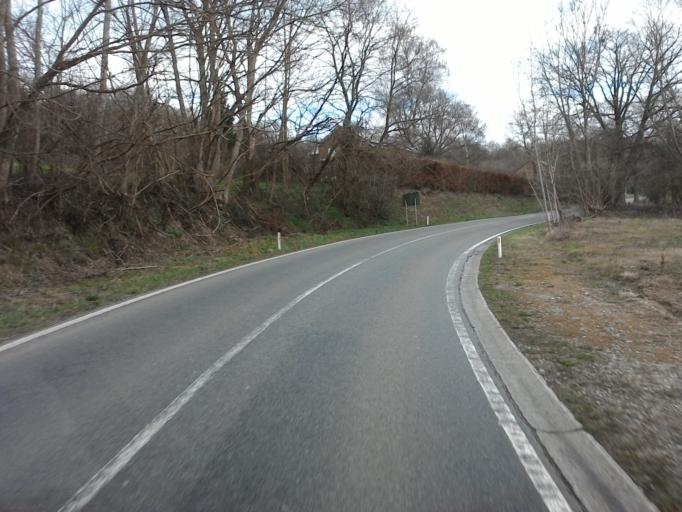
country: BE
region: Wallonia
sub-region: Province de Liege
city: Ferrieres
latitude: 50.4045
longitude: 5.6131
